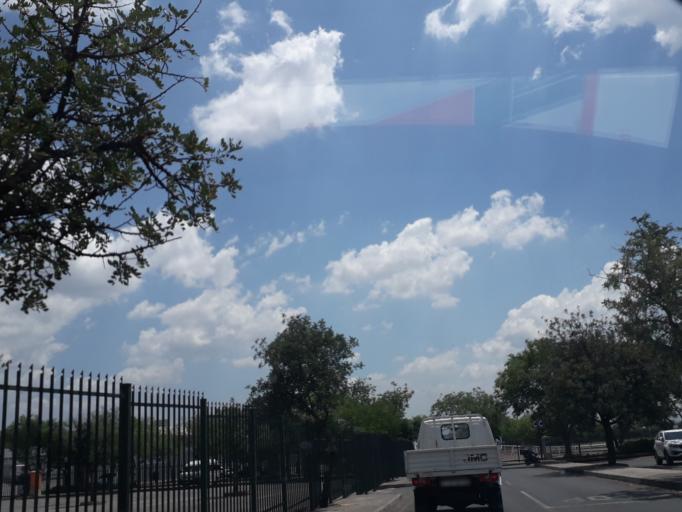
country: ZA
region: Gauteng
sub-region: West Rand District Municipality
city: Muldersdriseloop
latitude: -26.0630
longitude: 27.9448
